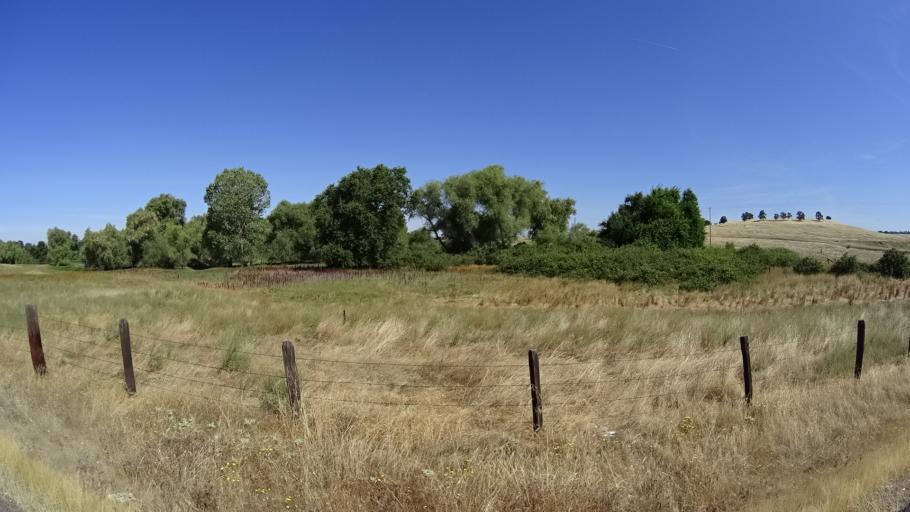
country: US
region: California
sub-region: Calaveras County
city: Valley Springs
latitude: 38.2294
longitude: -120.8359
